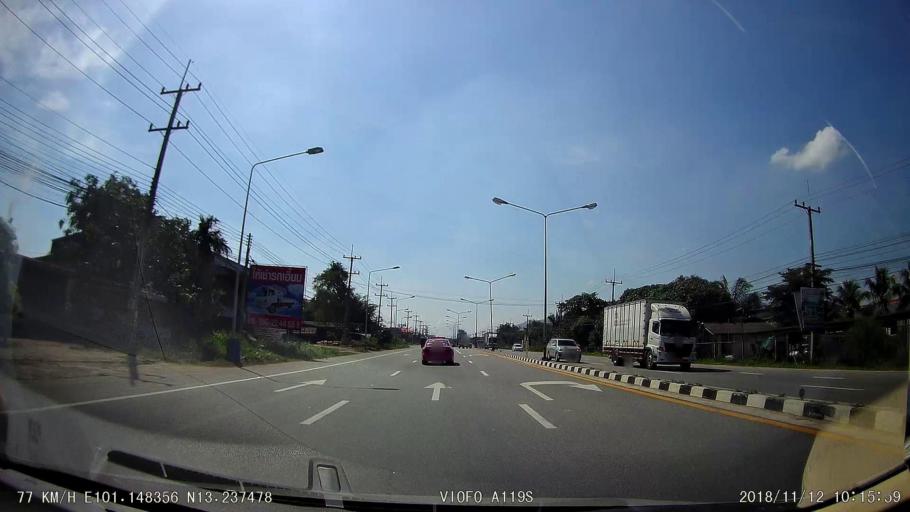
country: TH
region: Chon Buri
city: Ban Bueng
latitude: 13.2372
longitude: 101.1484
